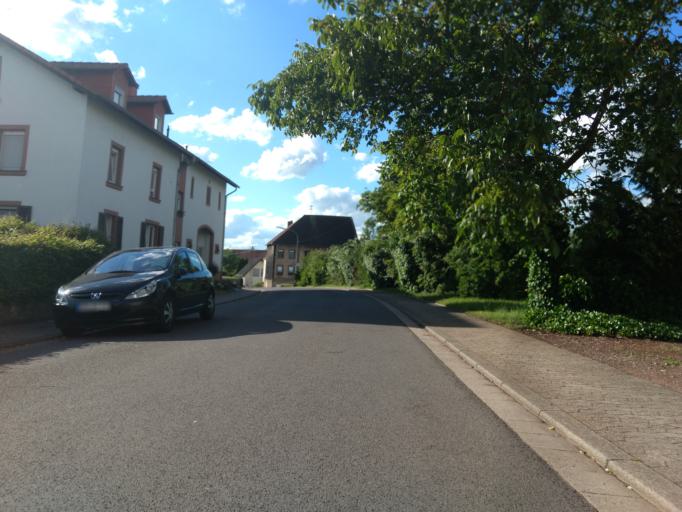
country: DE
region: Saarland
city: Merzig
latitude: 49.4468
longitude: 6.6130
